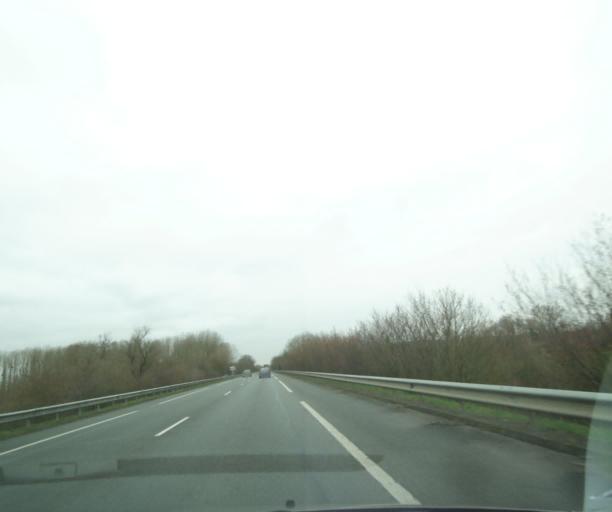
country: FR
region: Picardie
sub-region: Departement de l'Oise
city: Noyon
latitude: 49.5682
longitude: 3.0018
